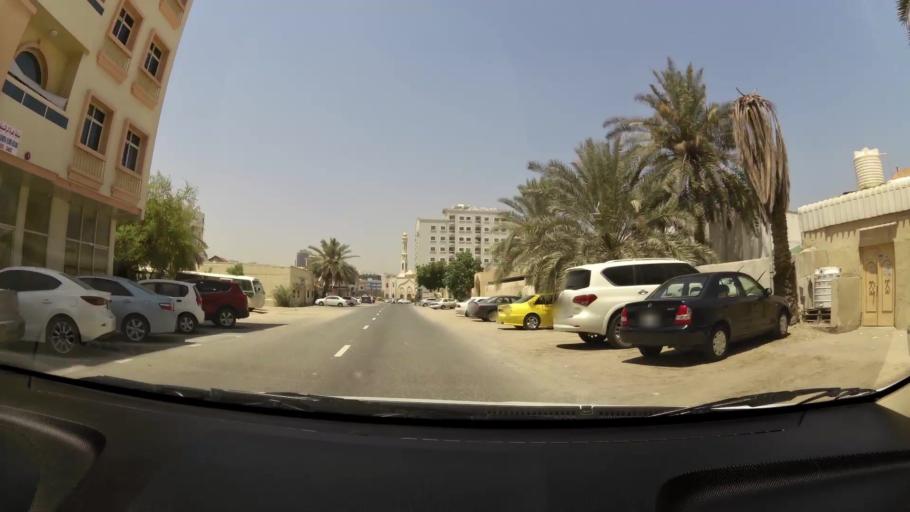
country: AE
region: Ajman
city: Ajman
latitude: 25.4021
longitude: 55.4466
